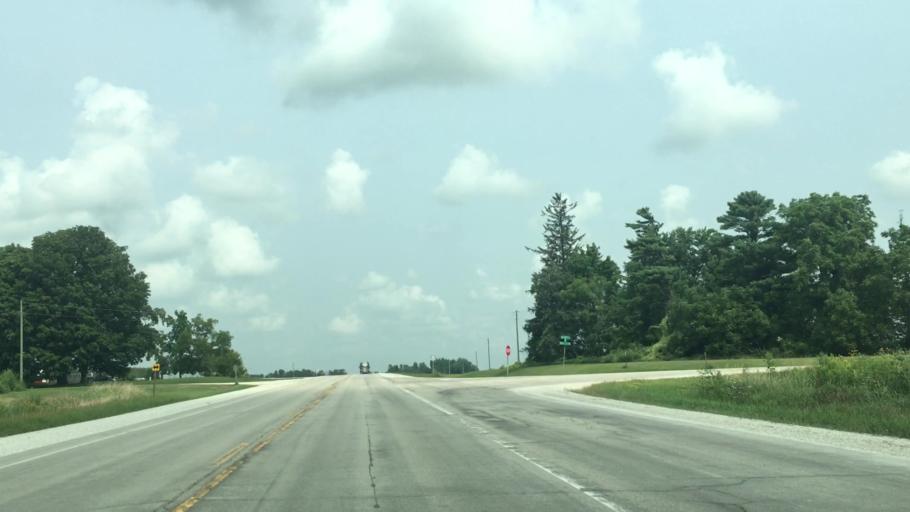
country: US
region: Minnesota
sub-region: Fillmore County
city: Harmony
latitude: 43.4719
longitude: -91.8700
